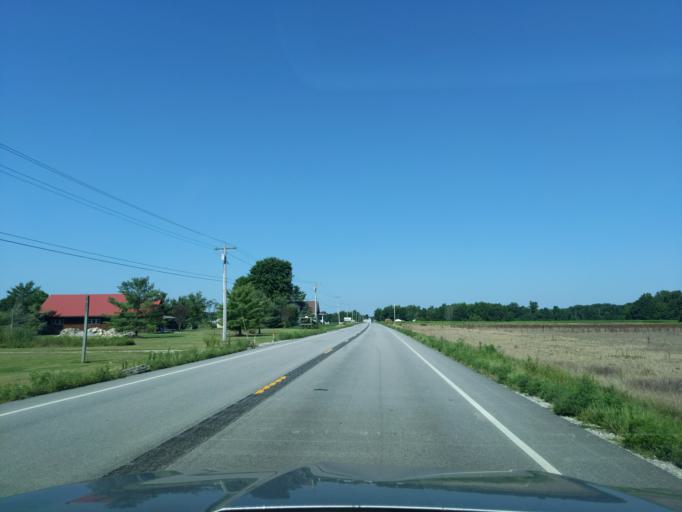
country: US
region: Indiana
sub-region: Ripley County
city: Versailles
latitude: 39.0748
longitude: -85.2975
